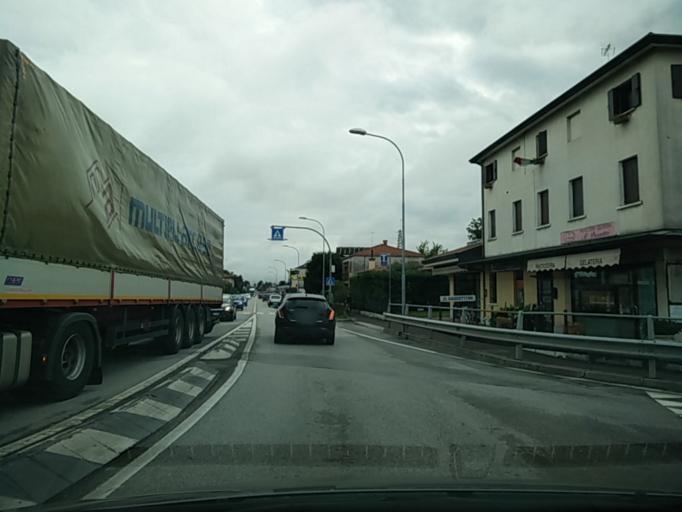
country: IT
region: Veneto
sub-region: Provincia di Padova
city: Cittadella
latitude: 45.6659
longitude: 11.7793
